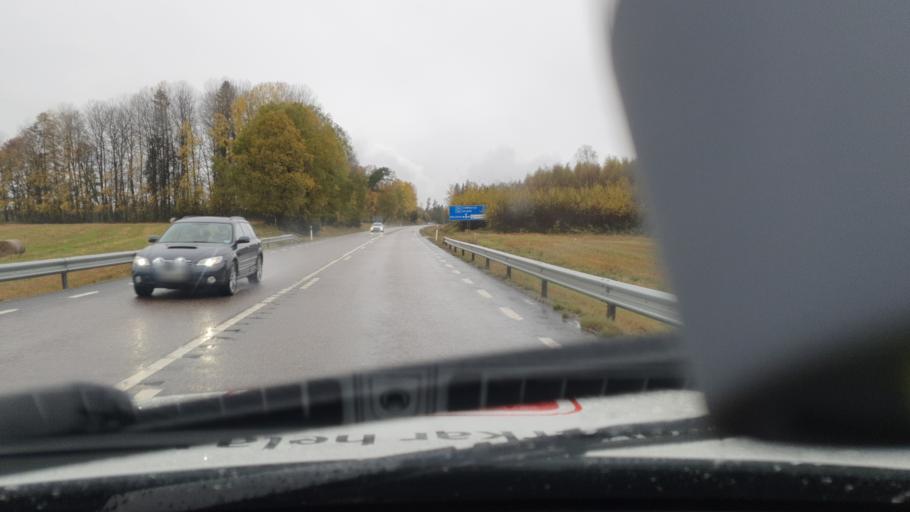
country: SE
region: Vaestra Goetaland
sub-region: Dals-Ed Kommun
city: Ed
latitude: 58.8988
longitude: 11.9688
